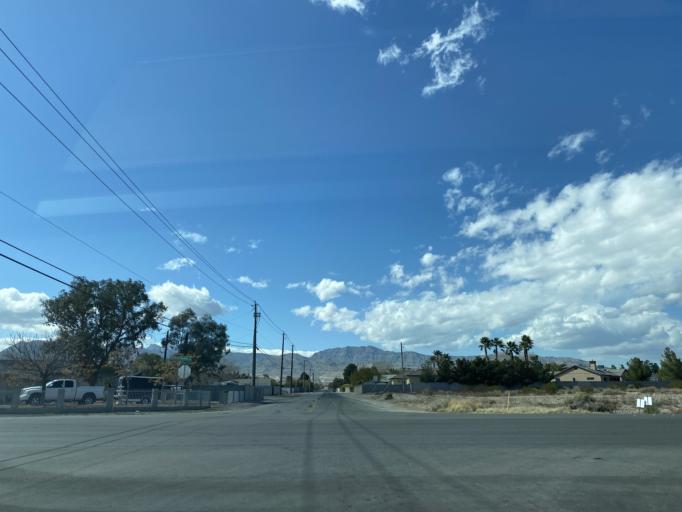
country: US
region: Nevada
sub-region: Clark County
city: Summerlin South
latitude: 36.2555
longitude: -115.2793
